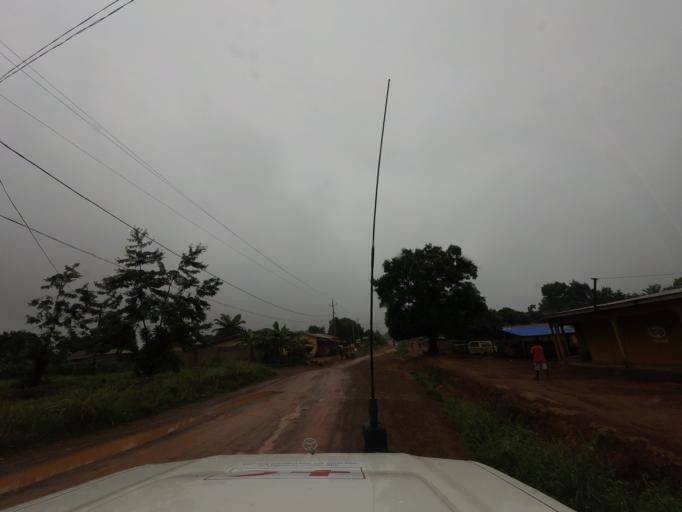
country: GN
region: Nzerekore
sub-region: Nzerekore Prefecture
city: Nzerekore
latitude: 7.7315
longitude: -8.8284
